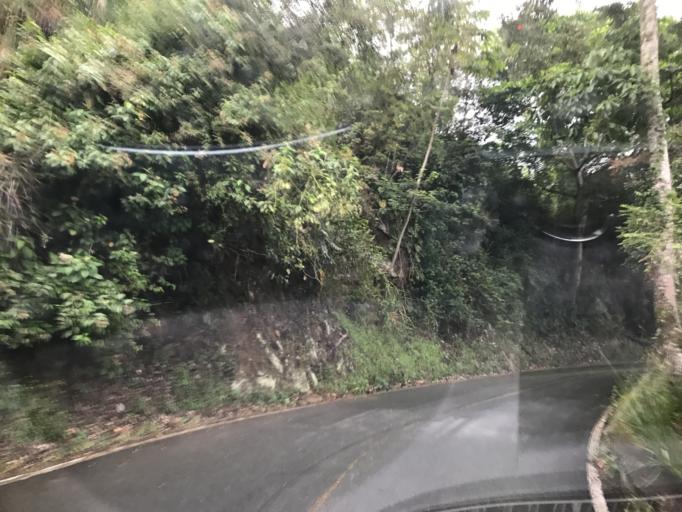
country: CO
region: Quindio
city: Genova
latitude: 4.2889
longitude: -75.7845
